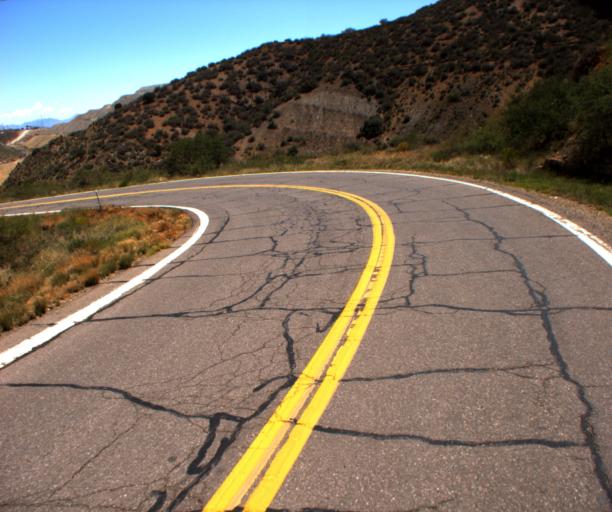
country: US
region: Arizona
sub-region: Greenlee County
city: Morenci
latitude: 33.0732
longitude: -109.3649
